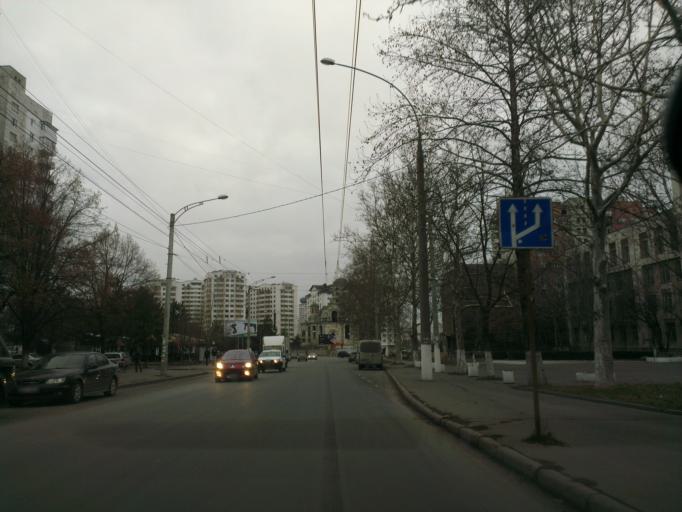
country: MD
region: Chisinau
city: Chisinau
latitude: 46.9851
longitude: 28.8460
